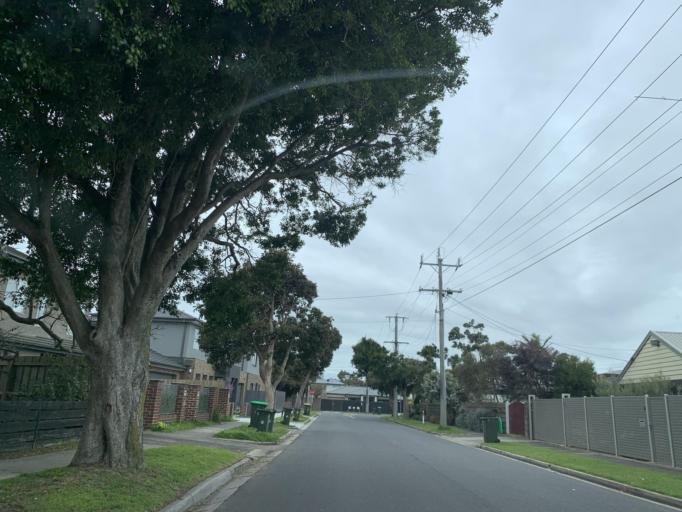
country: AU
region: Victoria
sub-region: Frankston
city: Seaford
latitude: -38.1079
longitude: 145.1307
